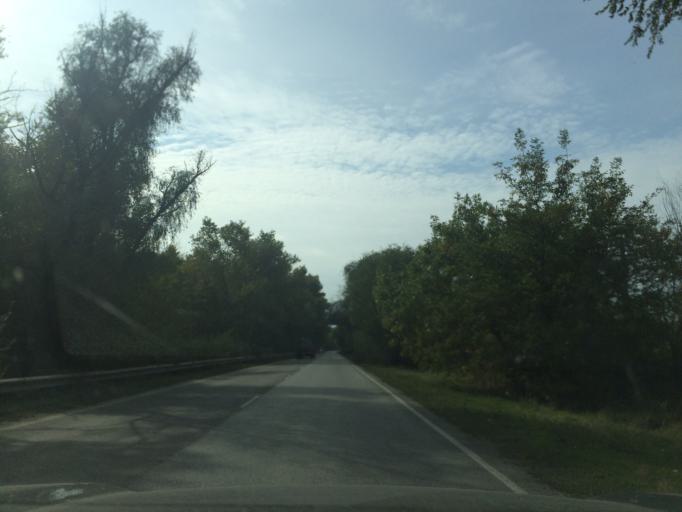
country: RU
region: Rostov
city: Kalinin
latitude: 47.1780
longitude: 39.5756
